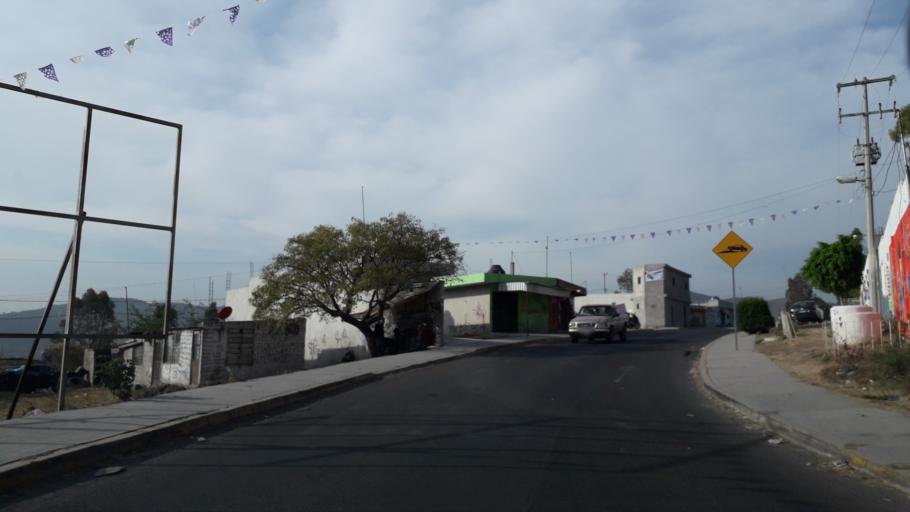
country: MX
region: Puebla
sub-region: Puebla
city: San Andres Azumiatla
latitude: 18.9107
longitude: -98.2415
